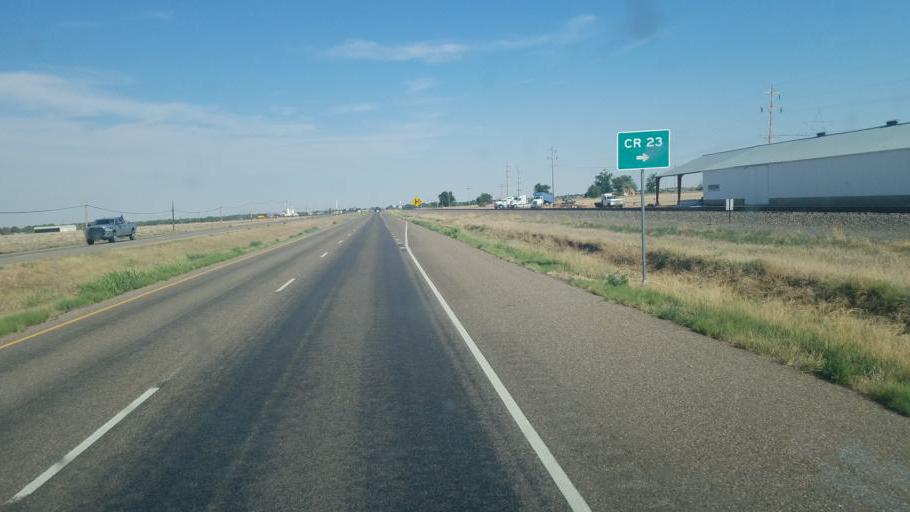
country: US
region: Colorado
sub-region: Otero County
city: Rocky Ford
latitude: 38.0283
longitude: -103.6589
